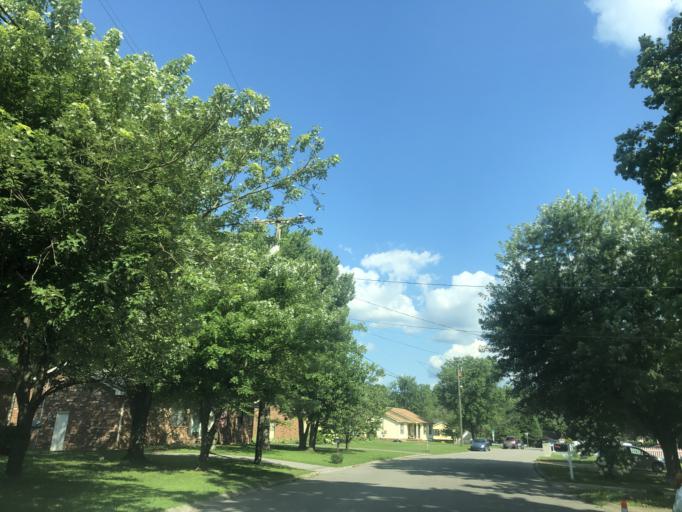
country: US
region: Tennessee
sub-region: Wilson County
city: Green Hill
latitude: 36.2053
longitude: -86.5969
